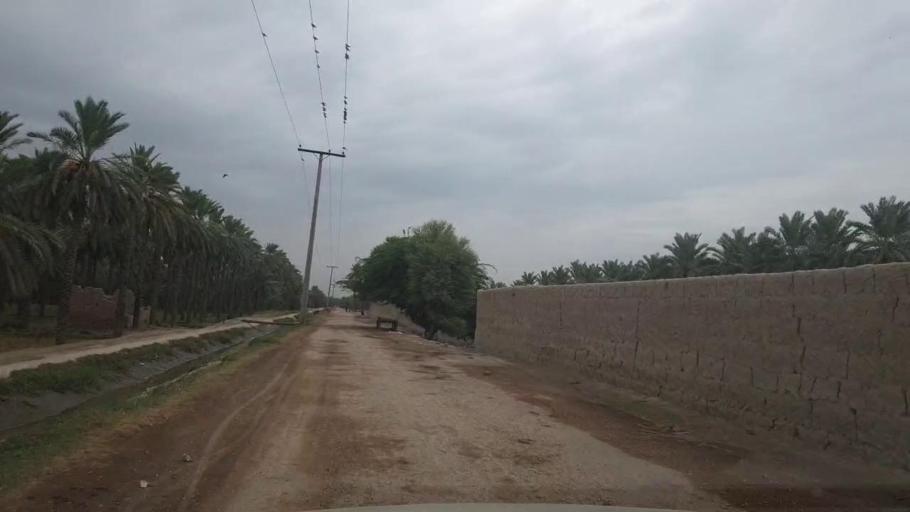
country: PK
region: Sindh
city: Khairpur
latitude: 27.6064
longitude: 68.8165
